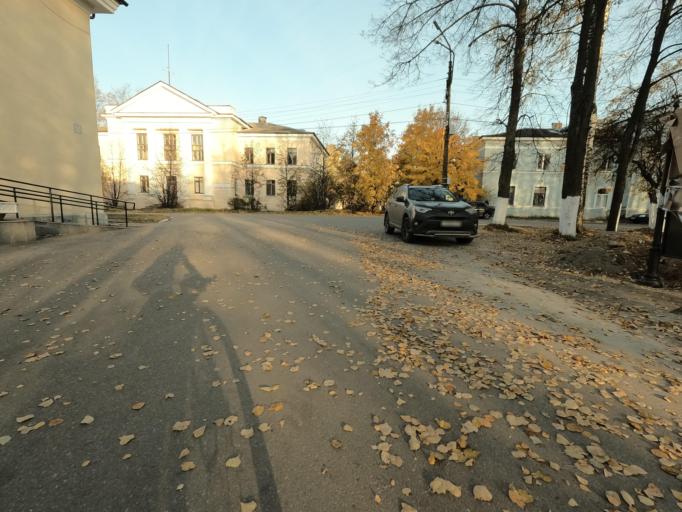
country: RU
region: Leningrad
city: Mga
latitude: 59.7581
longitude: 31.0637
